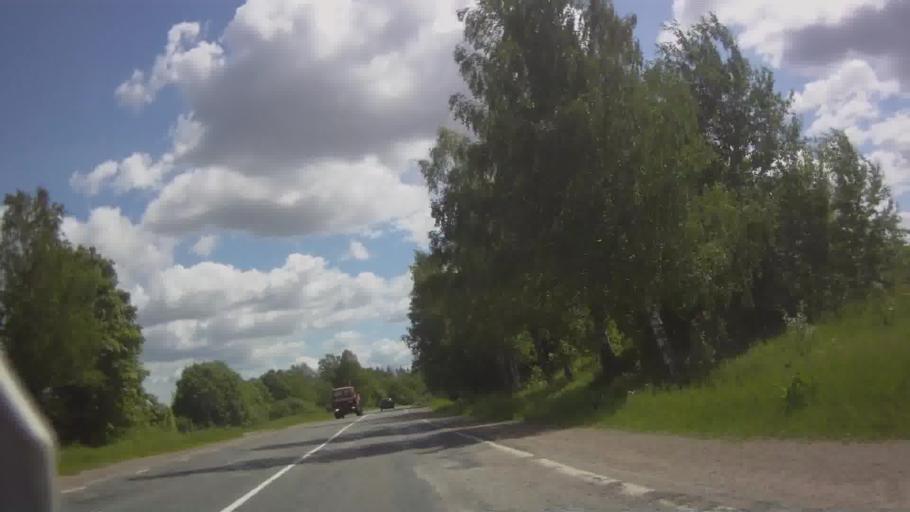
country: LV
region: Varaklani
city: Varaklani
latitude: 56.6094
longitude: 26.8403
